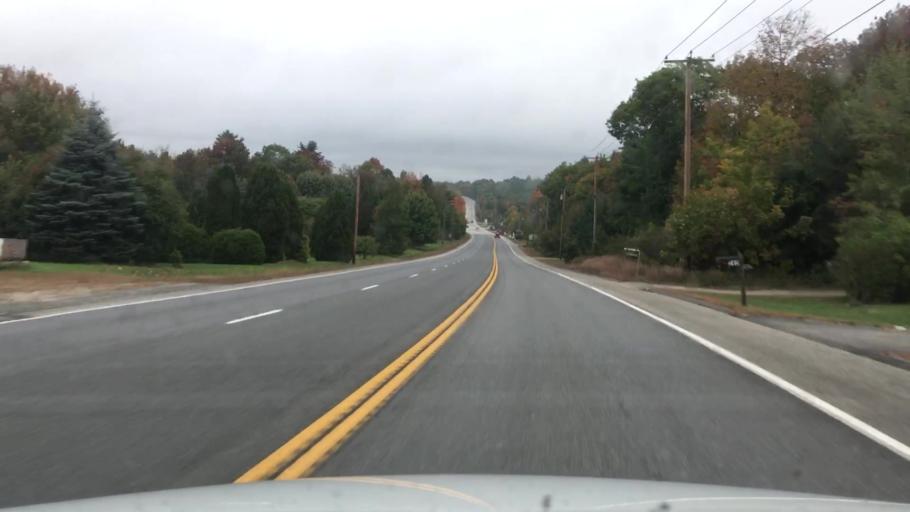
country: US
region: Maine
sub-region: Androscoggin County
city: Poland
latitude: 44.0073
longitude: -70.3620
